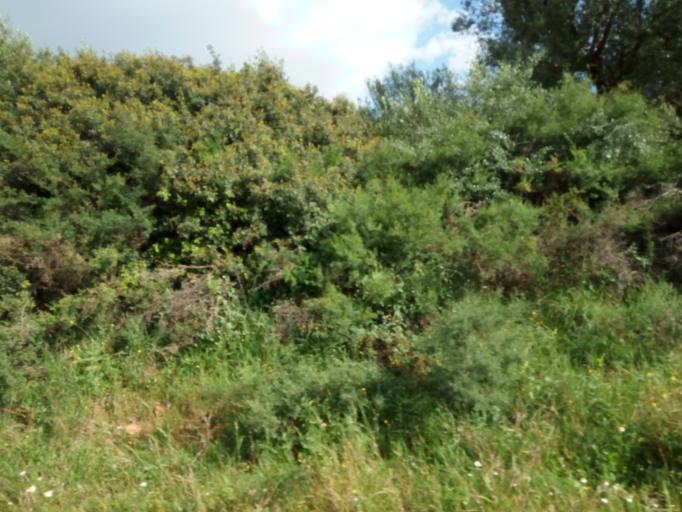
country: DZ
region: Tipaza
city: El Affroun
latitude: 36.3737
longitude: 2.5035
